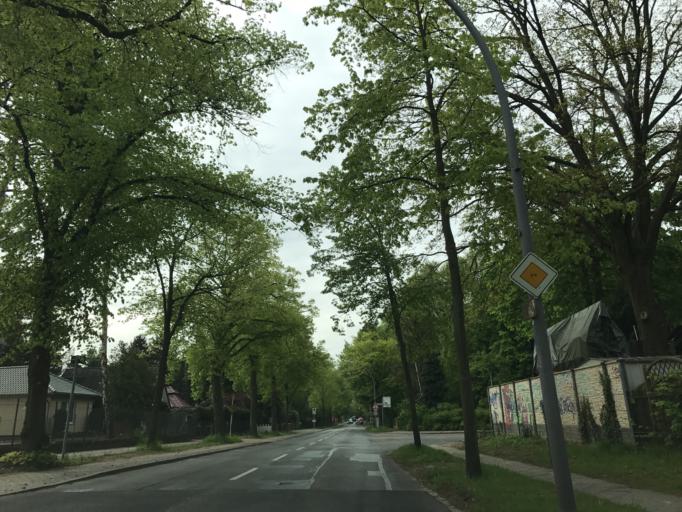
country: DE
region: Berlin
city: Kladow
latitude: 52.4663
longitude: 13.1284
